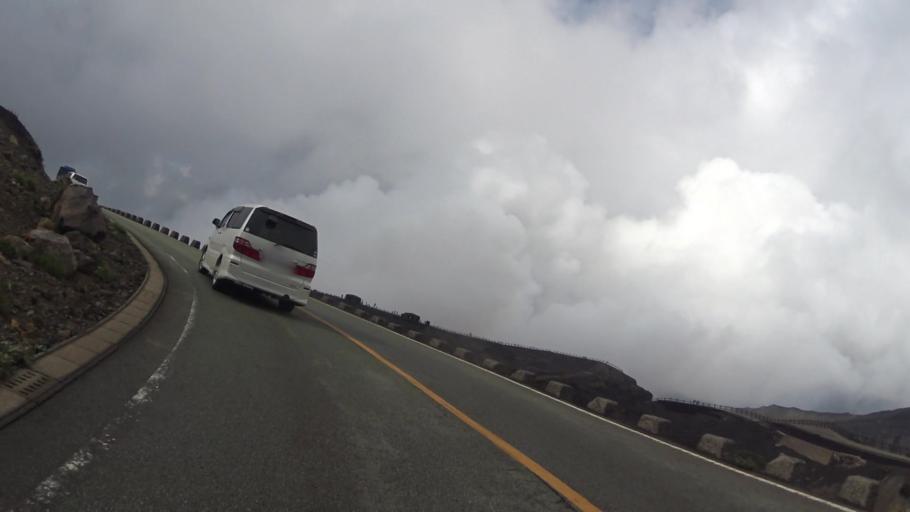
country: JP
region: Kumamoto
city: Aso
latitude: 32.8796
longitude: 131.0847
